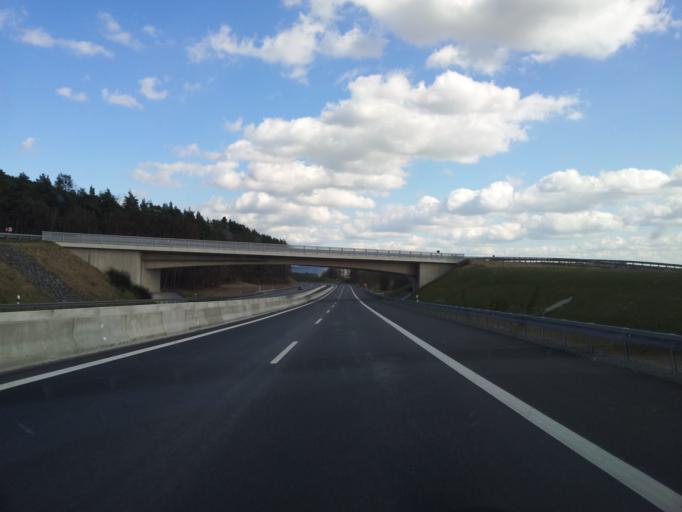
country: DE
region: Bavaria
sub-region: Upper Franconia
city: Neudrossenfeld
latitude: 50.0380
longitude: 11.5132
